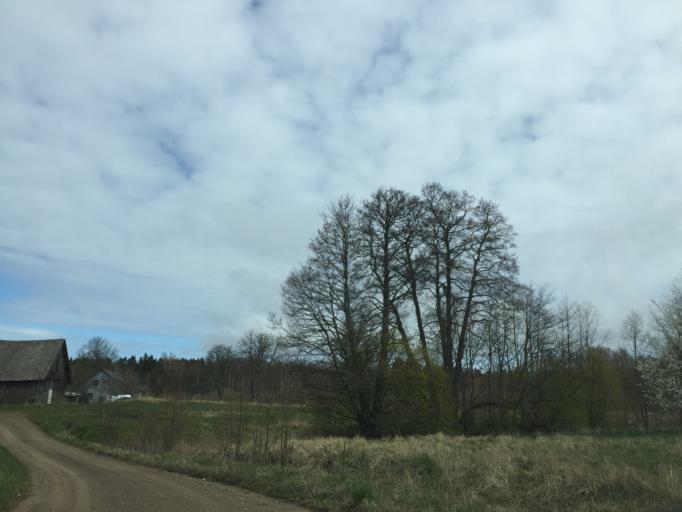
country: LV
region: Salacgrivas
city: Salacgriva
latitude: 57.5255
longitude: 24.3806
